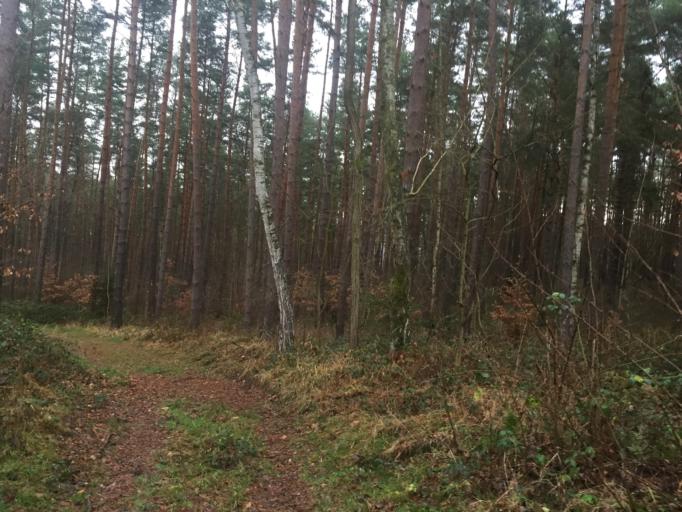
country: DE
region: Thuringia
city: Langenorla
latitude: 50.7178
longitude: 11.6004
